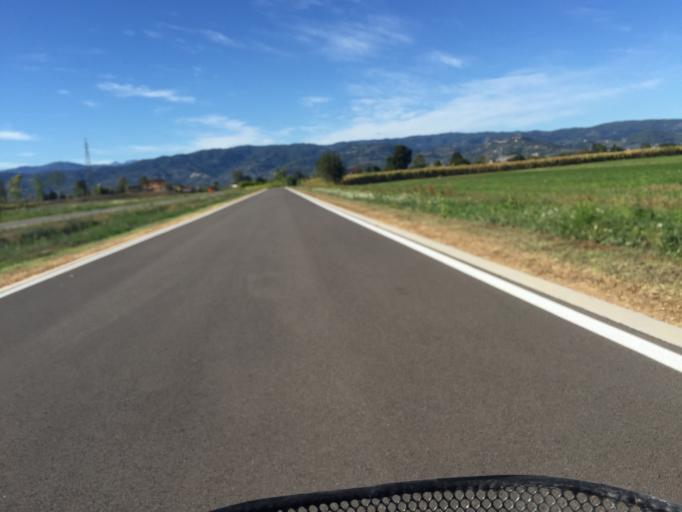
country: IT
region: Tuscany
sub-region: Provincia di Pistoia
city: Anchione
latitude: 43.8387
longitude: 10.7660
